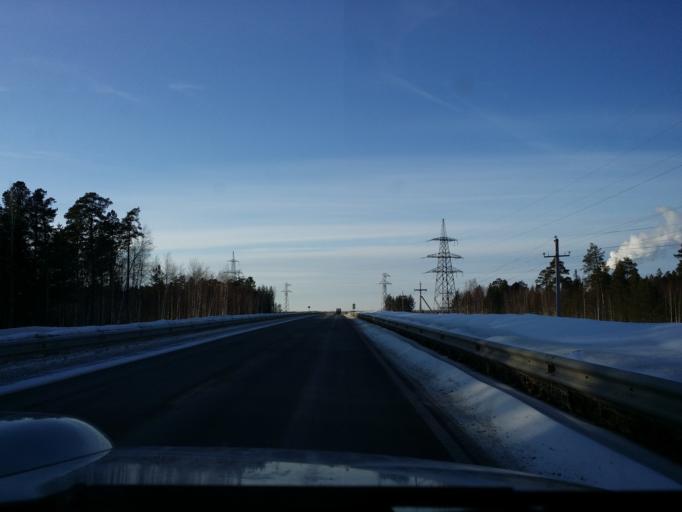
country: RU
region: Khanty-Mansiyskiy Avtonomnyy Okrug
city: Izluchinsk
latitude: 60.9317
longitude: 76.9871
